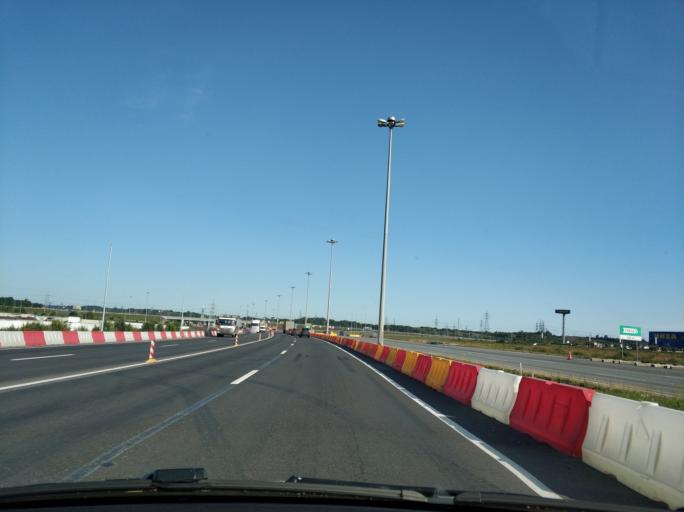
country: RU
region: Leningrad
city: Bugry
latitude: 60.0874
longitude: 30.3755
